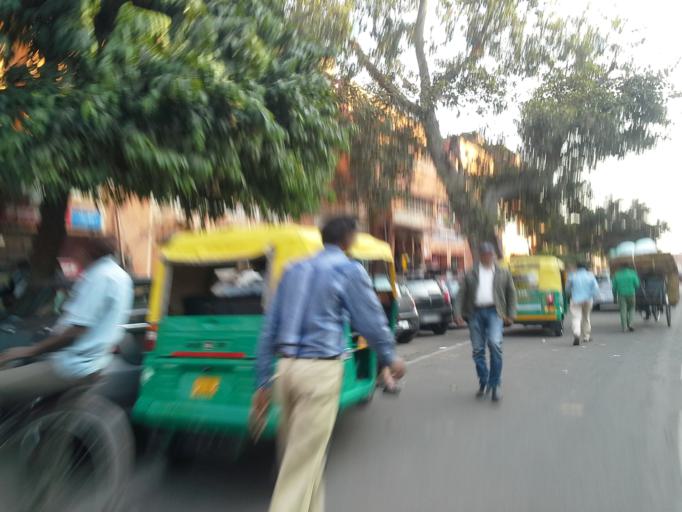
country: IN
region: Rajasthan
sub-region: Jaipur
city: Jaipur
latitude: 26.9188
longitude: 75.8214
